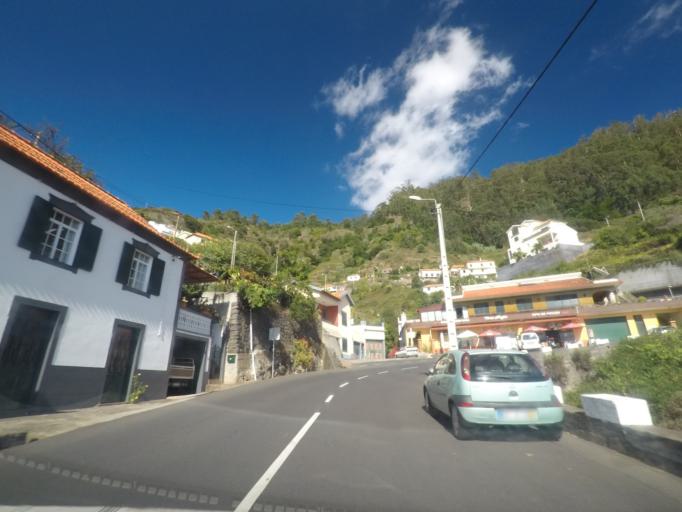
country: PT
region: Madeira
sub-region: Ribeira Brava
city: Campanario
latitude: 32.6730
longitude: -17.0223
